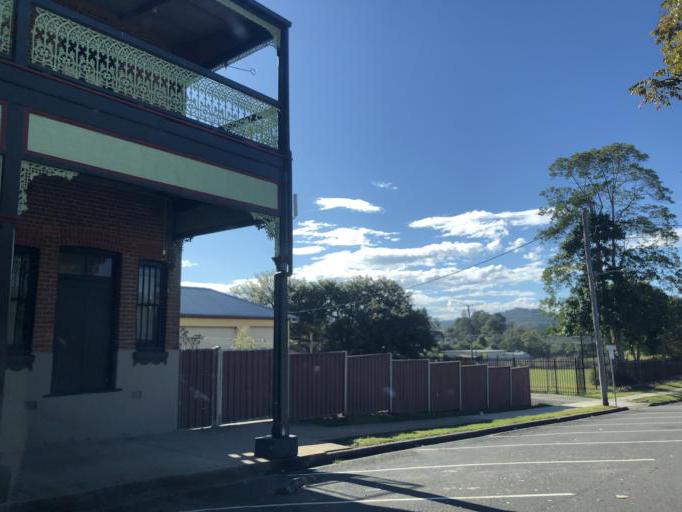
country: AU
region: New South Wales
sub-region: Nambucca Shire
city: Bowraville
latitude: -30.6465
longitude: 152.8532
